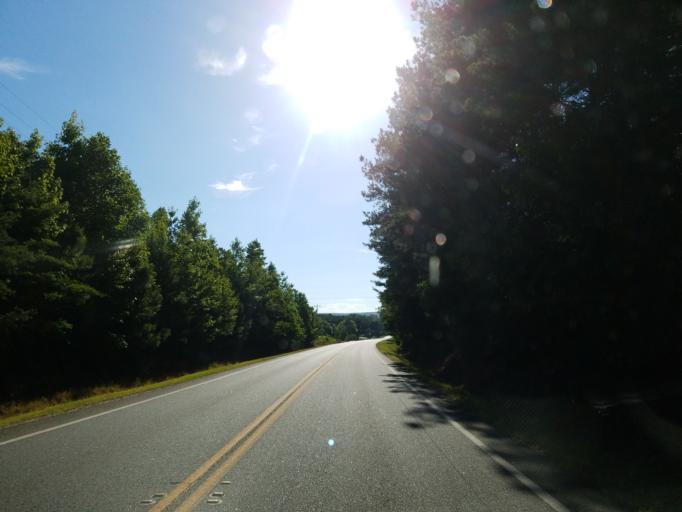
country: US
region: Georgia
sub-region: Gordon County
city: Calhoun
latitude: 34.5725
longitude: -84.9766
